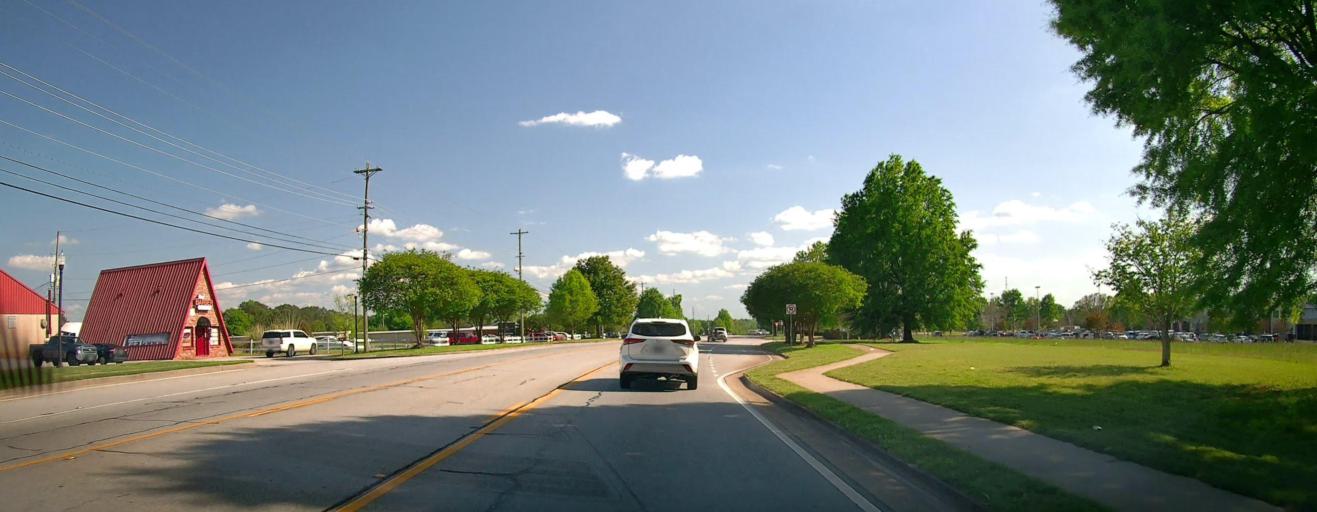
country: US
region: Georgia
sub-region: Morgan County
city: Madison
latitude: 33.5755
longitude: -83.4772
